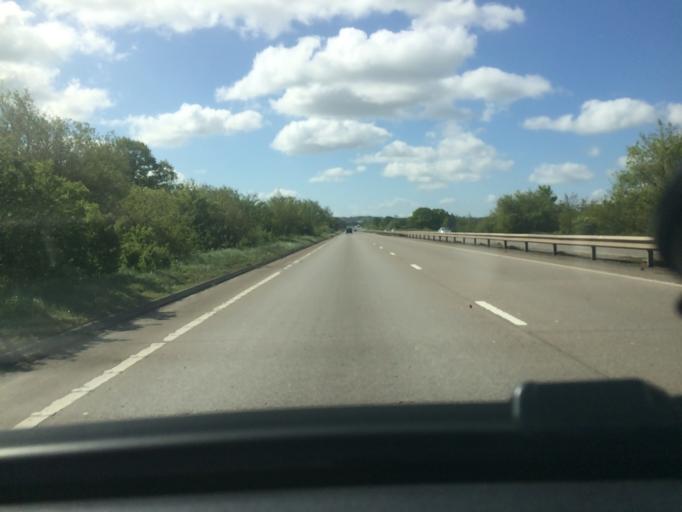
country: GB
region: Wales
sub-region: Wrexham
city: Rossett
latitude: 53.1295
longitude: -2.9477
